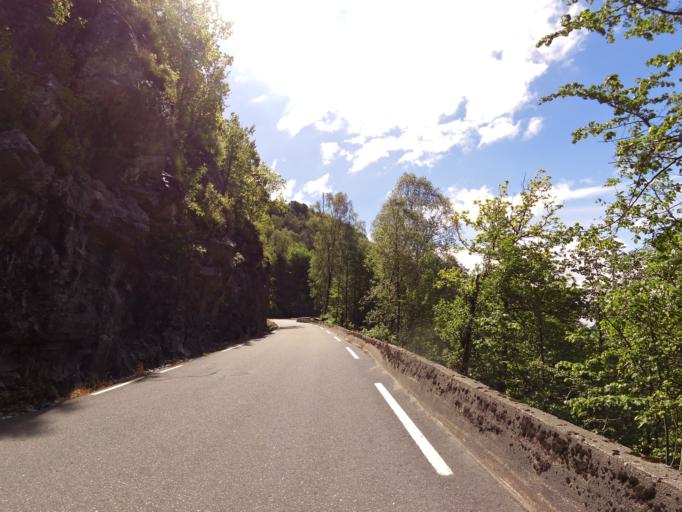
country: NO
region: Vest-Agder
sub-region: Kvinesdal
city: Liknes
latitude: 58.2940
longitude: 6.9441
